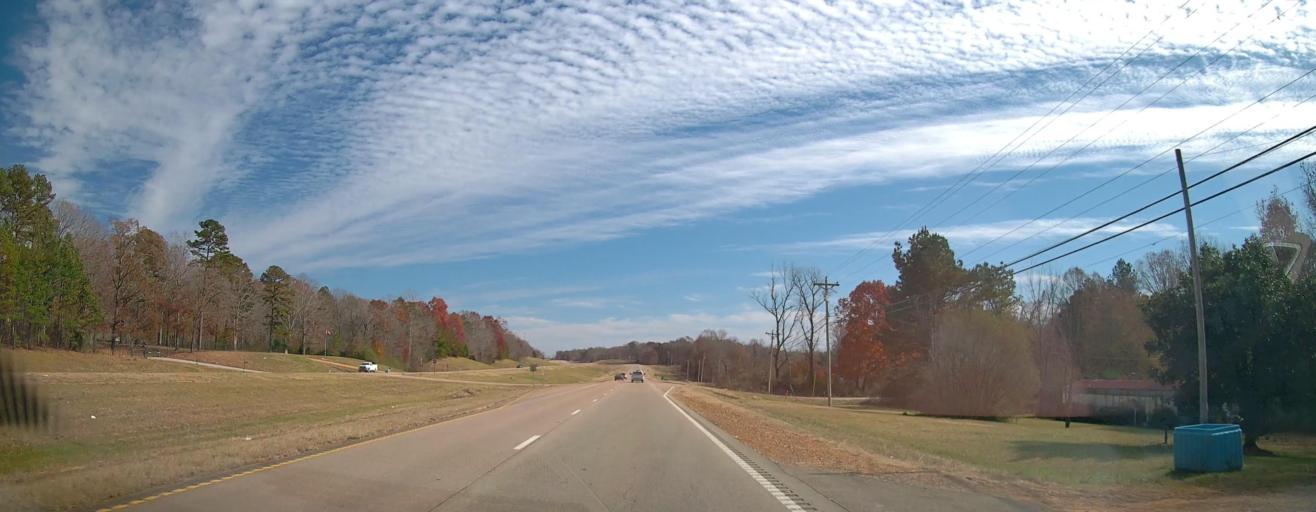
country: US
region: Mississippi
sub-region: Tippah County
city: Ripley
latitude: 34.9520
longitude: -88.8321
